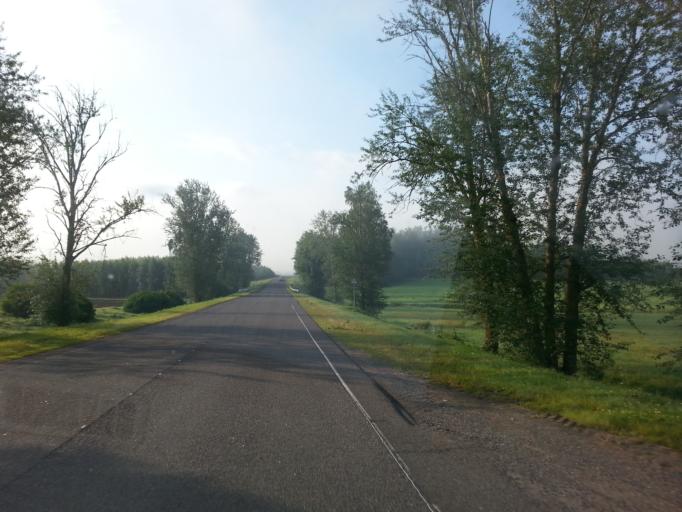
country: BY
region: Minsk
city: Kryvichy
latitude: 54.7388
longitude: 27.1315
